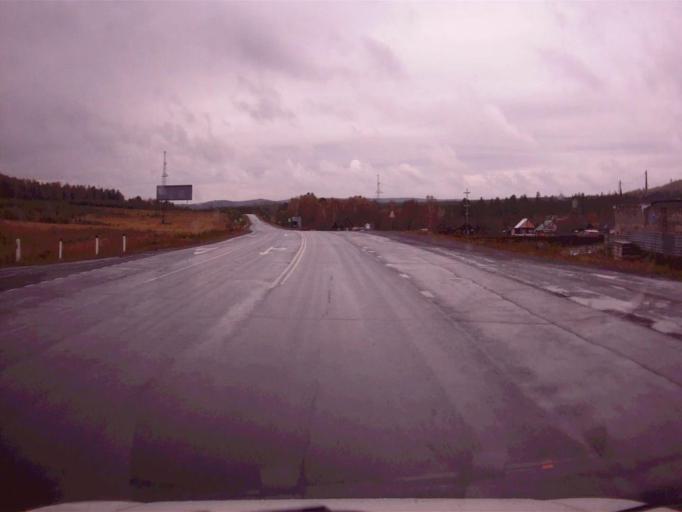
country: RU
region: Chelyabinsk
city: Verkhniy Ufaley
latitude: 56.0037
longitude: 60.3284
